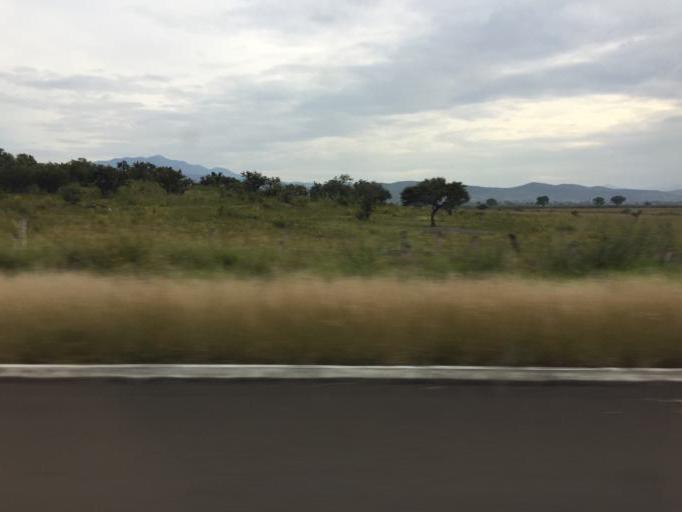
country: MX
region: Mexico
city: Huaniqueo de Morales
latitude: 19.8894
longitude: -101.5245
